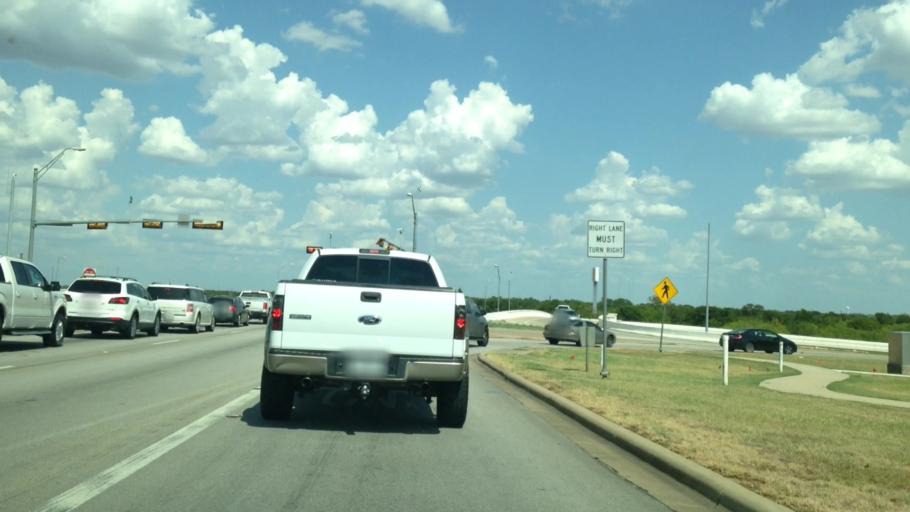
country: US
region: Texas
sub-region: Williamson County
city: Georgetown
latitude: 30.6330
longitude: -97.6930
